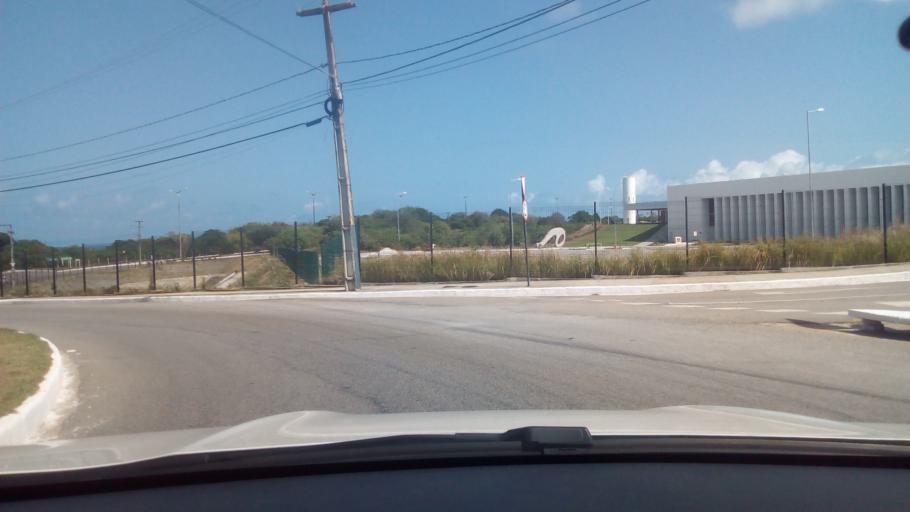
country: BR
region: Paraiba
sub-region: Joao Pessoa
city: Joao Pessoa
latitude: -7.1500
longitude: -34.7987
